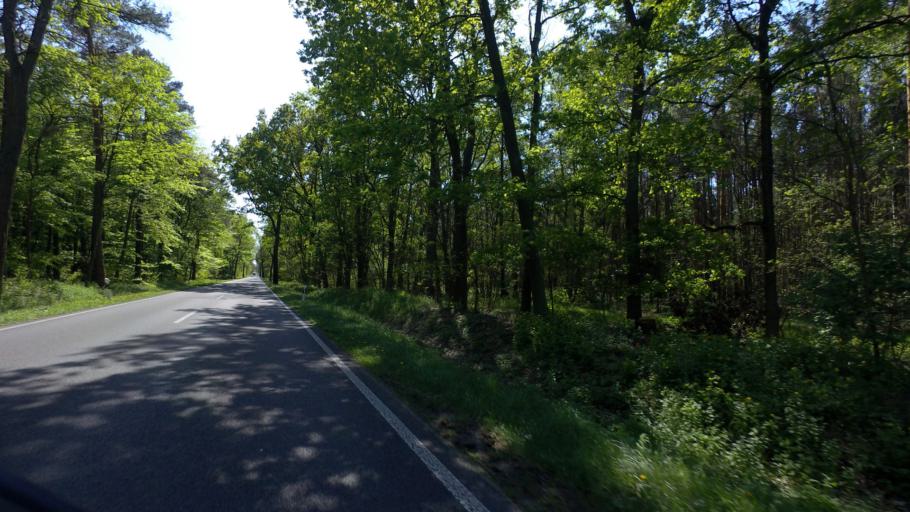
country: DE
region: Brandenburg
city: Tauche
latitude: 52.1093
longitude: 14.1860
